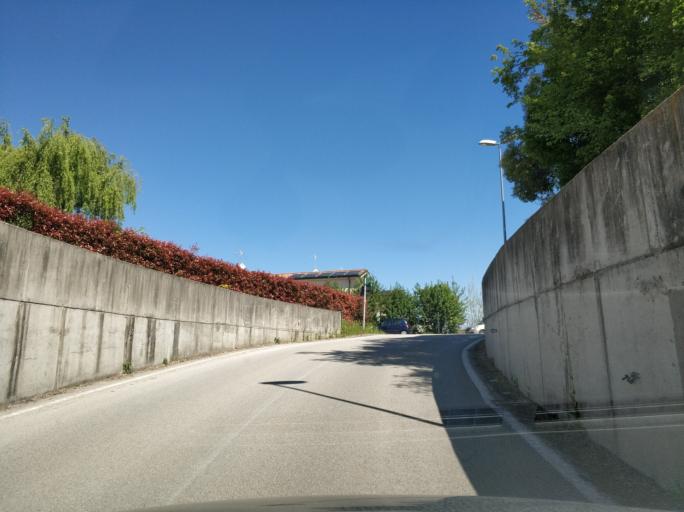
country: IT
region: Veneto
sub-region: Provincia di Venezia
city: Pianiga
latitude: 45.4396
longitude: 11.9998
